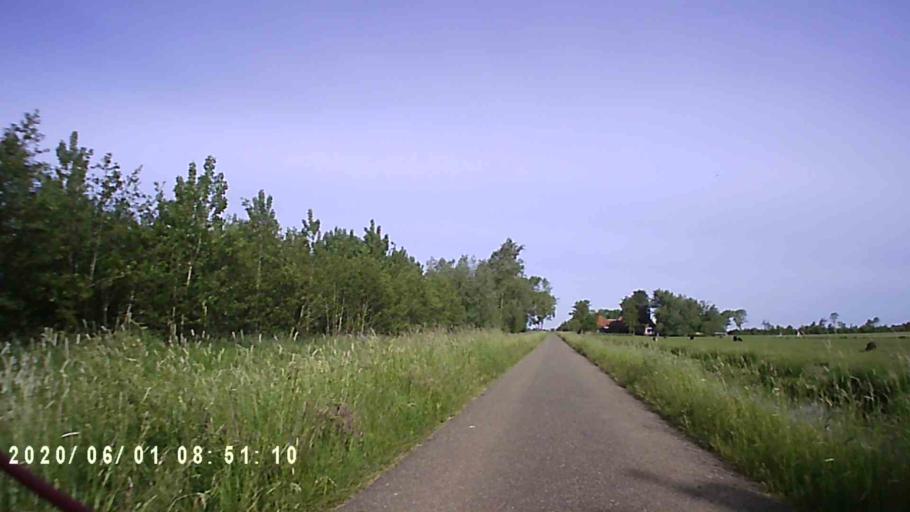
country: NL
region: Friesland
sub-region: Gemeente Ferwerderadiel
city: Burdaard
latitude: 53.2754
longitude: 5.8382
